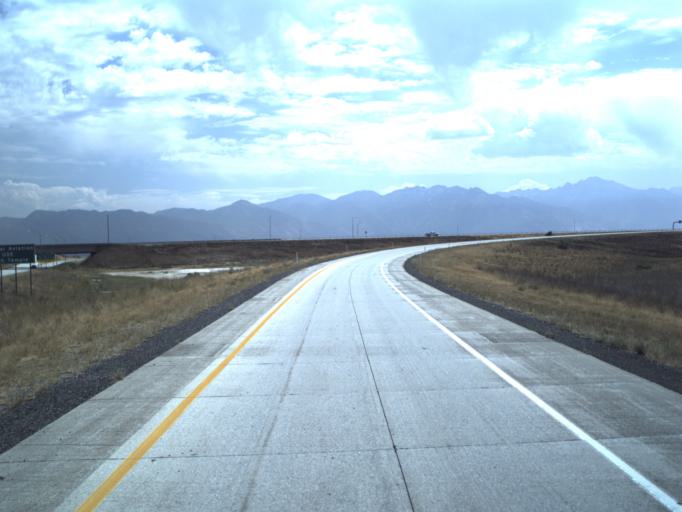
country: US
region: Utah
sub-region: Salt Lake County
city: West Valley City
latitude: 40.7644
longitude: -111.9914
